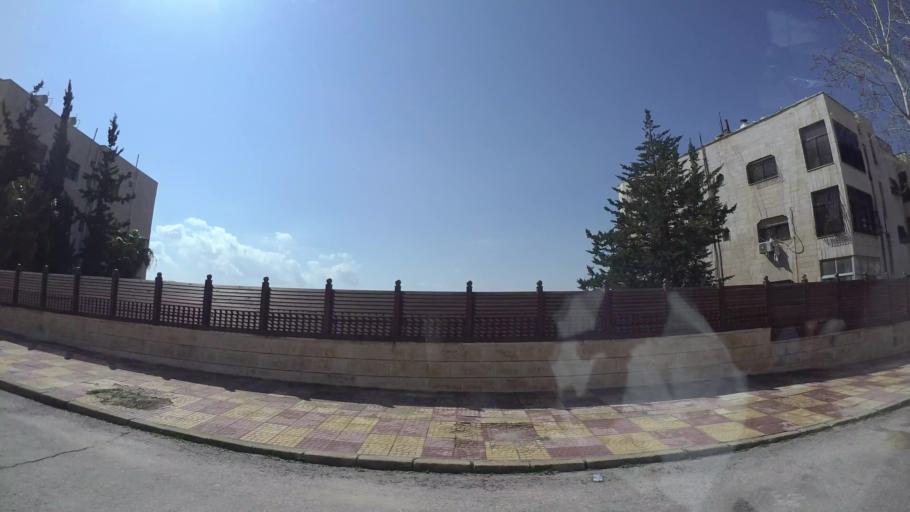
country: JO
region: Amman
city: Al Jubayhah
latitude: 31.9919
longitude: 35.8969
